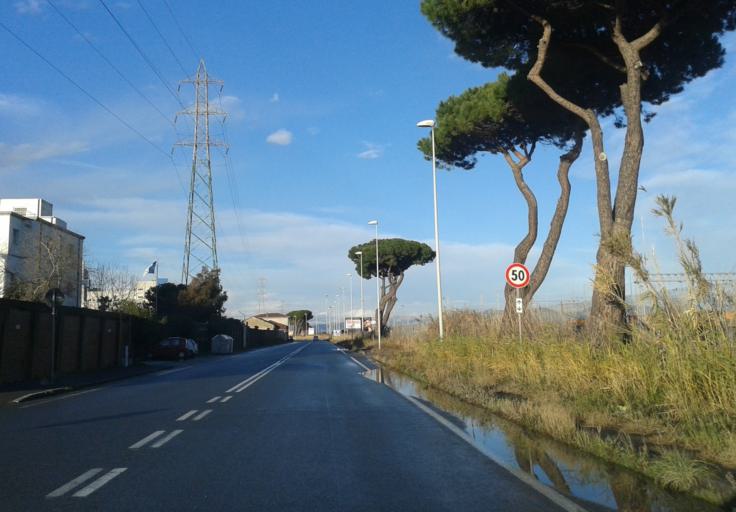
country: IT
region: Tuscany
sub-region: Provincia di Livorno
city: Livorno
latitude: 43.5742
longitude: 10.3201
